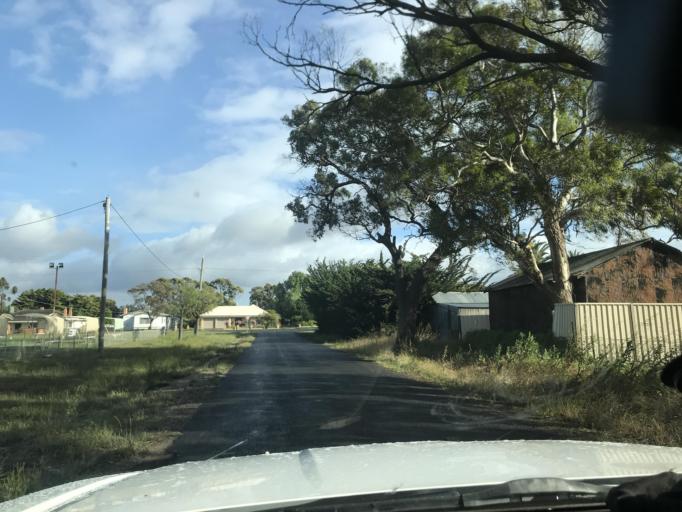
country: AU
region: Victoria
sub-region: Horsham
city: Horsham
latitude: -36.7201
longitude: 141.4704
